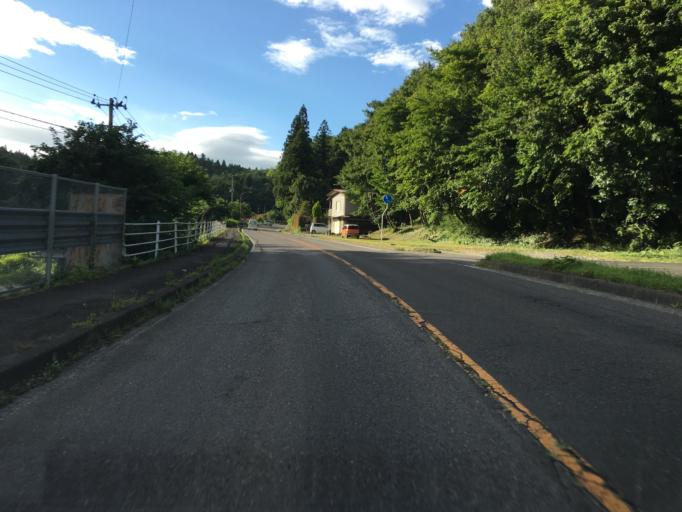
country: JP
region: Fukushima
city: Nihommatsu
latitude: 37.6381
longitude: 140.4644
